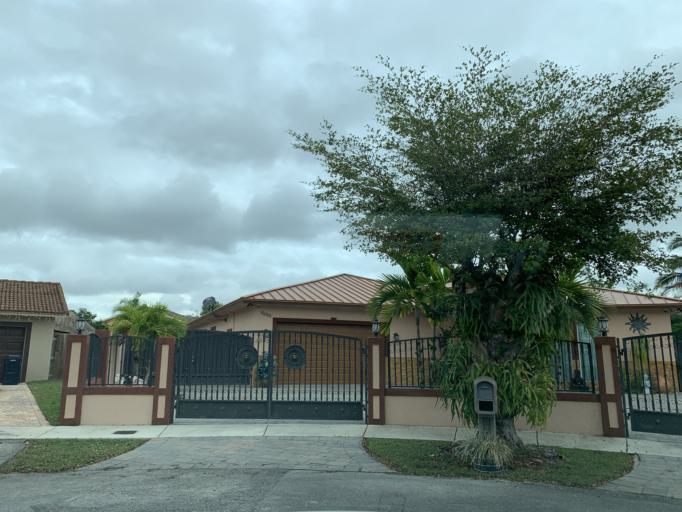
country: US
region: Florida
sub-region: Miami-Dade County
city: Kendall West
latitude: 25.7024
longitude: -80.4380
